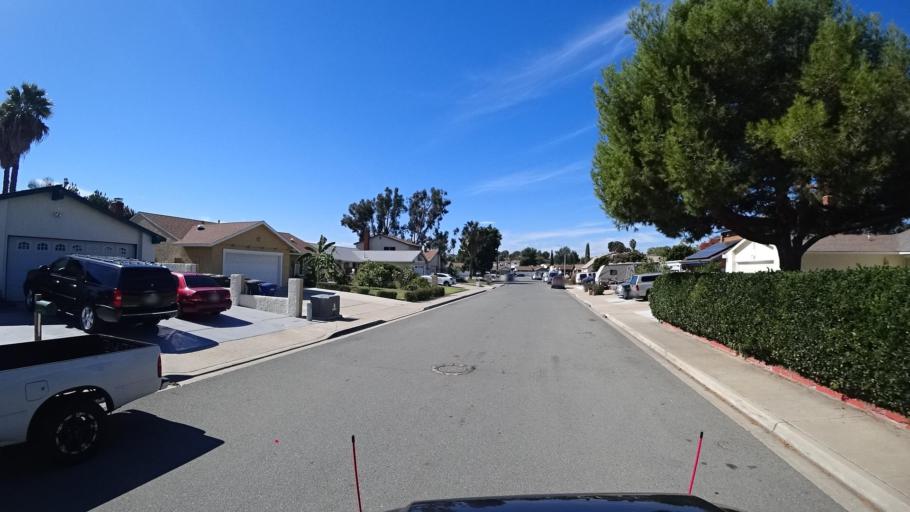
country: US
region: California
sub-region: San Diego County
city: La Presa
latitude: 32.7082
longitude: -116.9852
